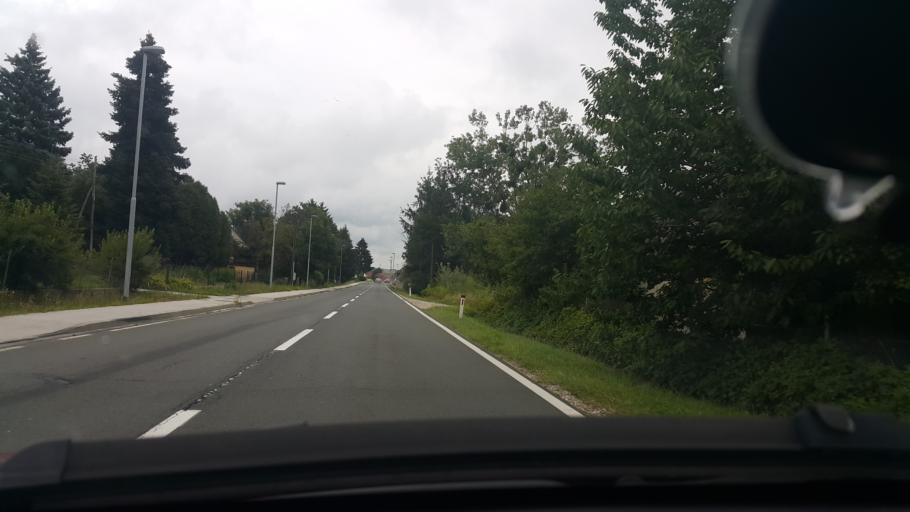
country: SI
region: Zavrc
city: Zavrc
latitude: 46.4161
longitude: 16.0855
